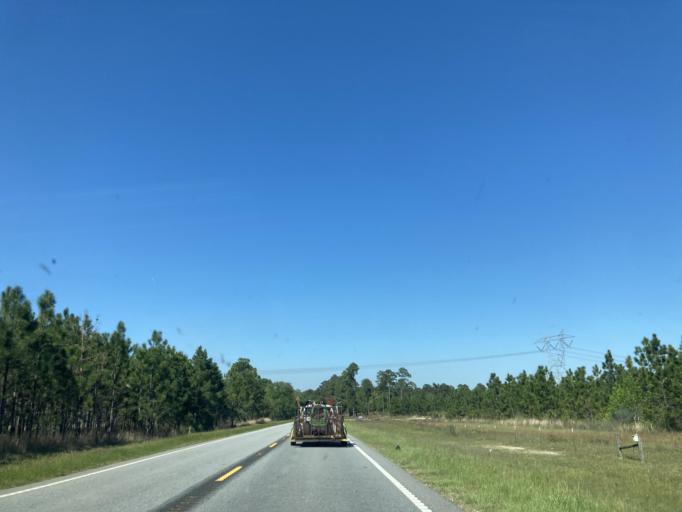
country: US
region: Georgia
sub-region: Baker County
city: Newton
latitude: 31.3463
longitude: -84.3063
